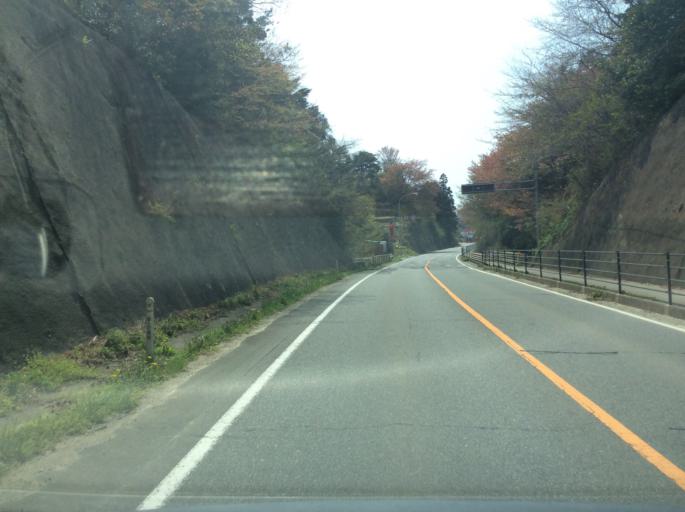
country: JP
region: Fukushima
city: Iwaki
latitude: 37.2168
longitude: 140.9996
